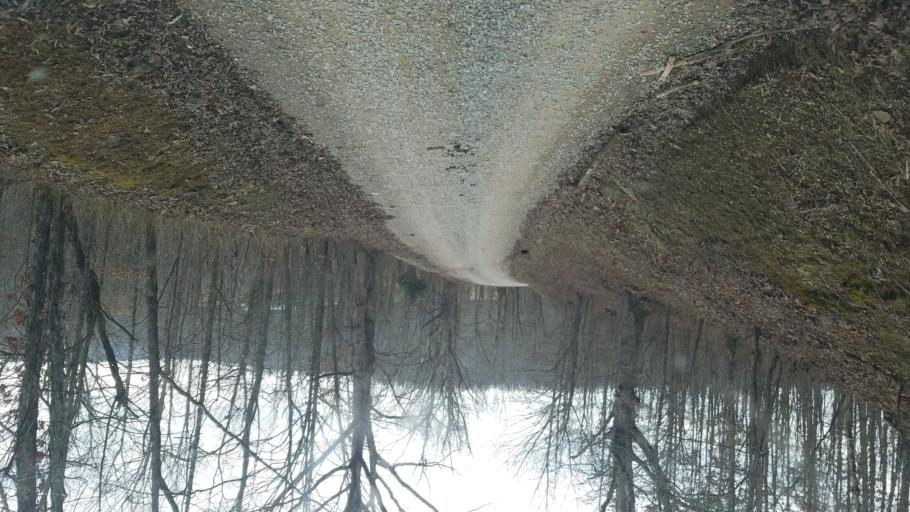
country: US
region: Ohio
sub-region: Gallia County
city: Gallipolis
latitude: 38.7341
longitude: -82.3197
